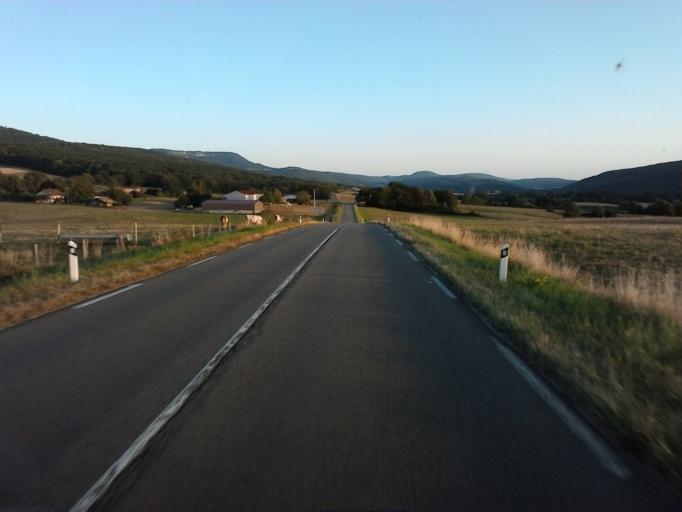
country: FR
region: Franche-Comte
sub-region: Departement du Doubs
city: Quingey
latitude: 47.0440
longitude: 5.8756
